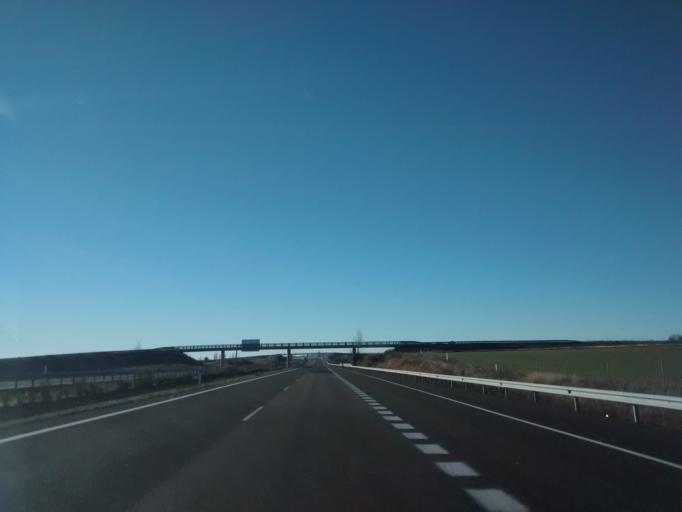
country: ES
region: Castille and Leon
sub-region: Provincia de Palencia
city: Santa Cruz de Boedo
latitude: 42.5365
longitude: -4.3807
